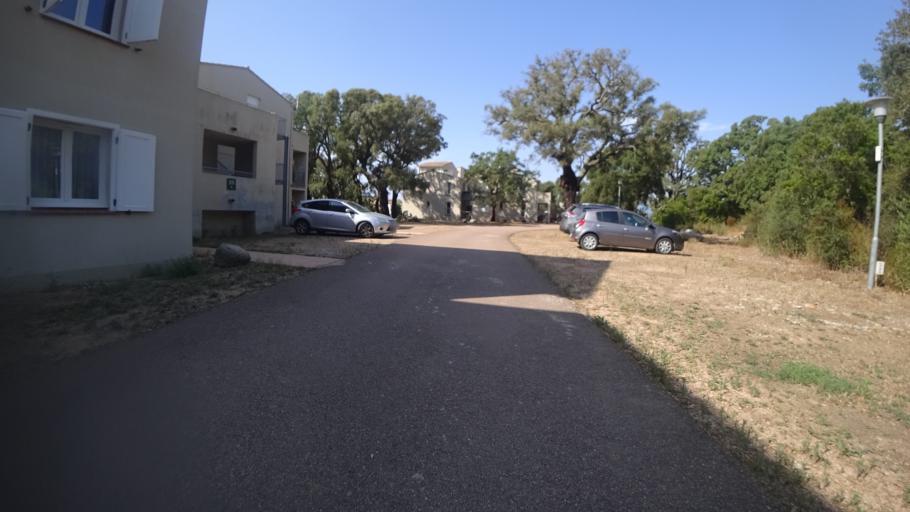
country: FR
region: Corsica
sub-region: Departement de la Corse-du-Sud
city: Porto-Vecchio
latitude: 41.6521
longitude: 9.3291
